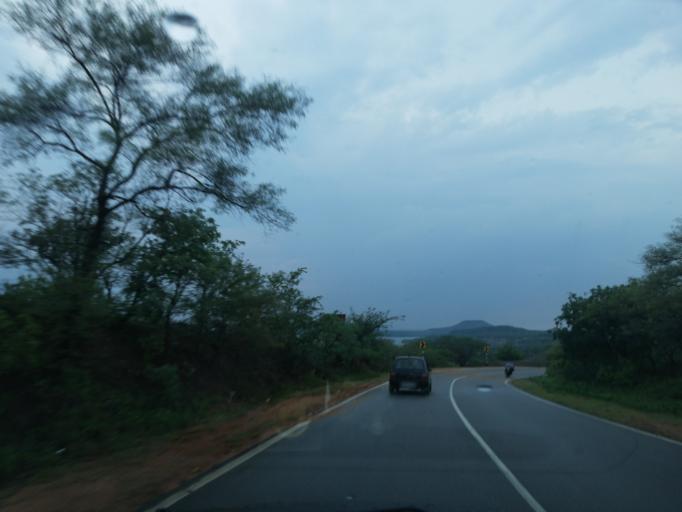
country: IN
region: Andhra Pradesh
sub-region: Guntur
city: Macherla
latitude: 16.6334
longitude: 79.2870
